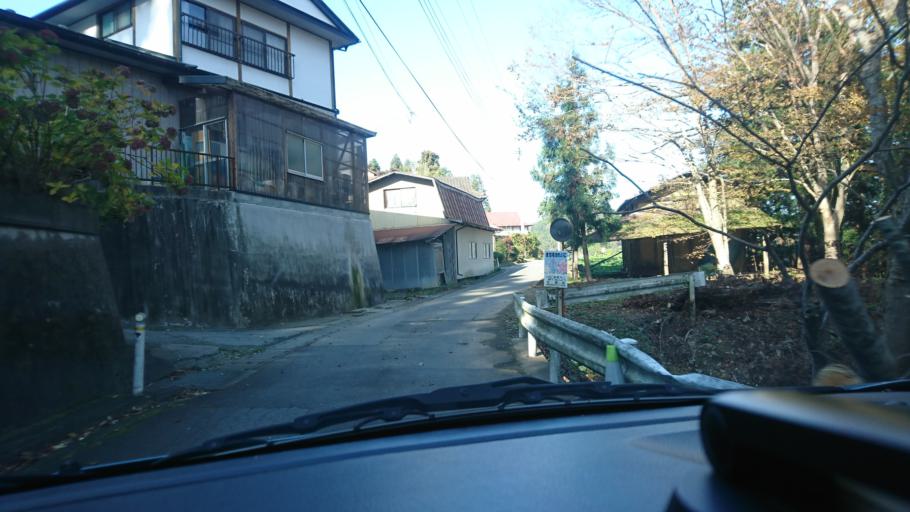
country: JP
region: Iwate
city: Ichinoseki
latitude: 38.8273
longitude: 141.2493
